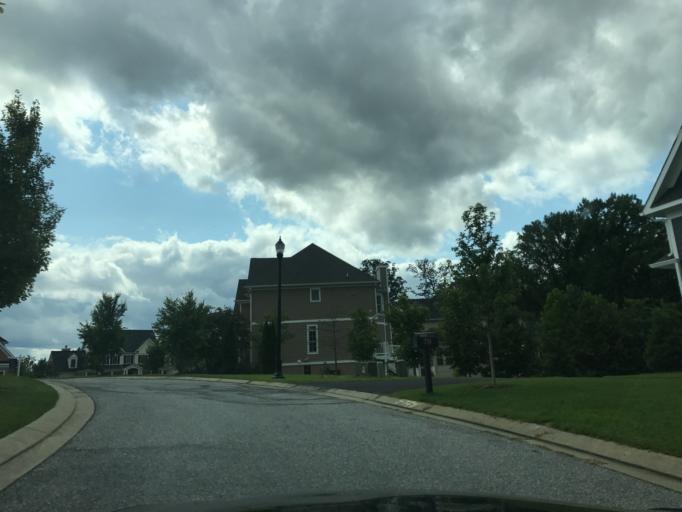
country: US
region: Maryland
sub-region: Baltimore County
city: Lutherville
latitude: 39.4124
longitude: -76.6330
